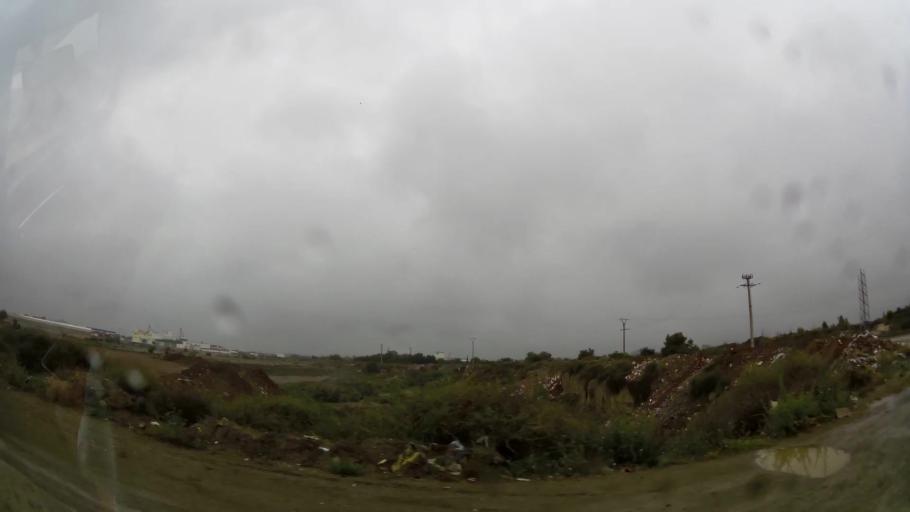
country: MA
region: Taza-Al Hoceima-Taounate
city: Imzourene
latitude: 35.1521
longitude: -3.8191
